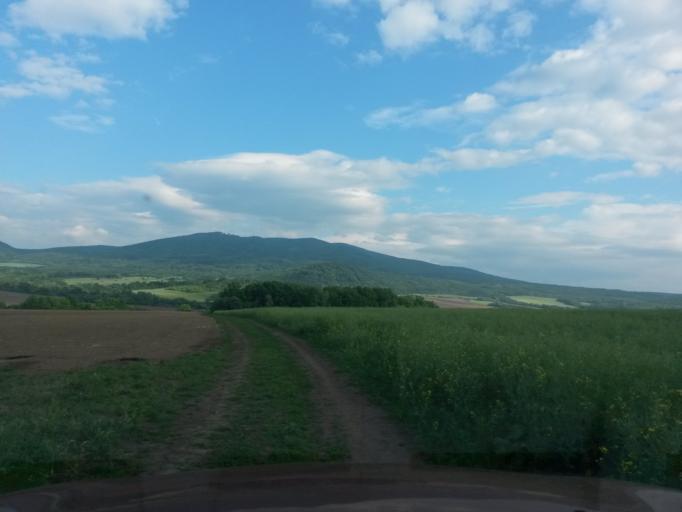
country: SK
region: Kosicky
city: Secovce
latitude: 48.7452
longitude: 21.4641
